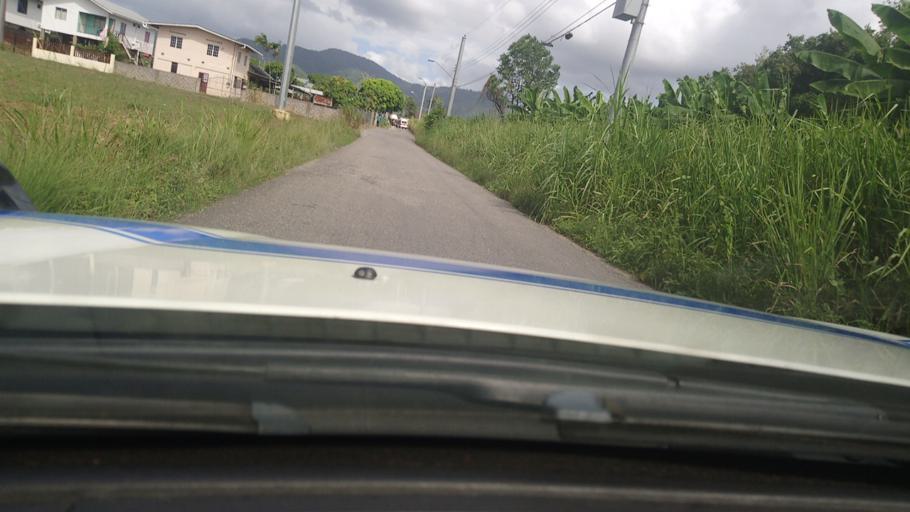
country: TT
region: Borough of Arima
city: Arima
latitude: 10.6230
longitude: -61.3018
